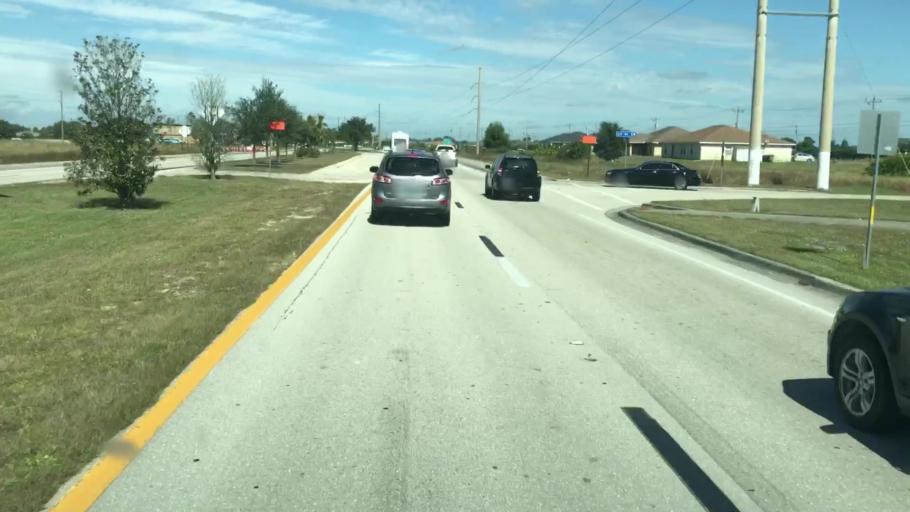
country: US
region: Florida
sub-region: Lee County
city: Gateway
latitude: 26.5871
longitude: -81.7122
